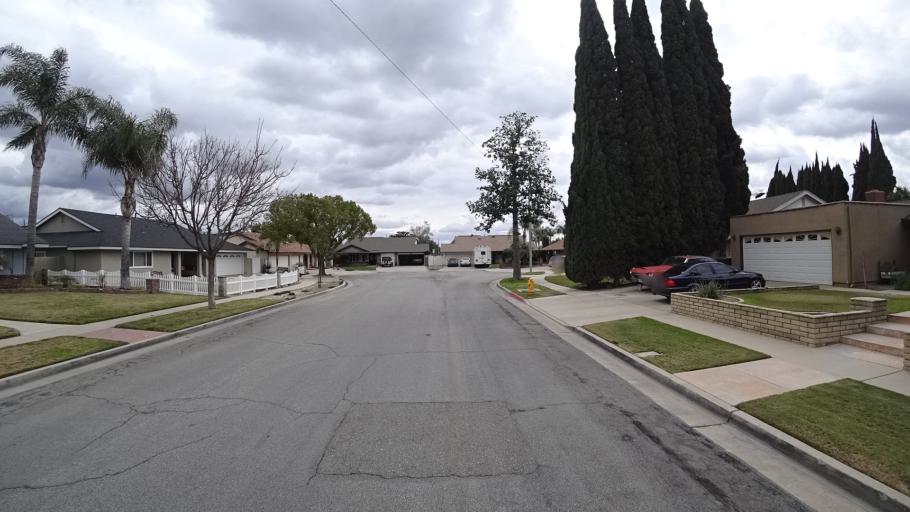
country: US
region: California
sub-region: Orange County
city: Placentia
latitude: 33.8413
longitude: -117.8678
